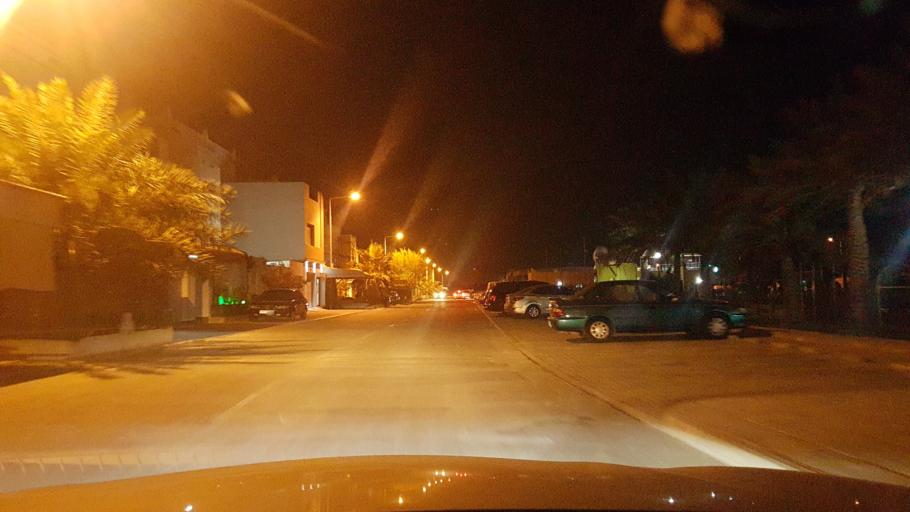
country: BH
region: Central Governorate
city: Madinat Hamad
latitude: 26.0967
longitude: 50.4792
